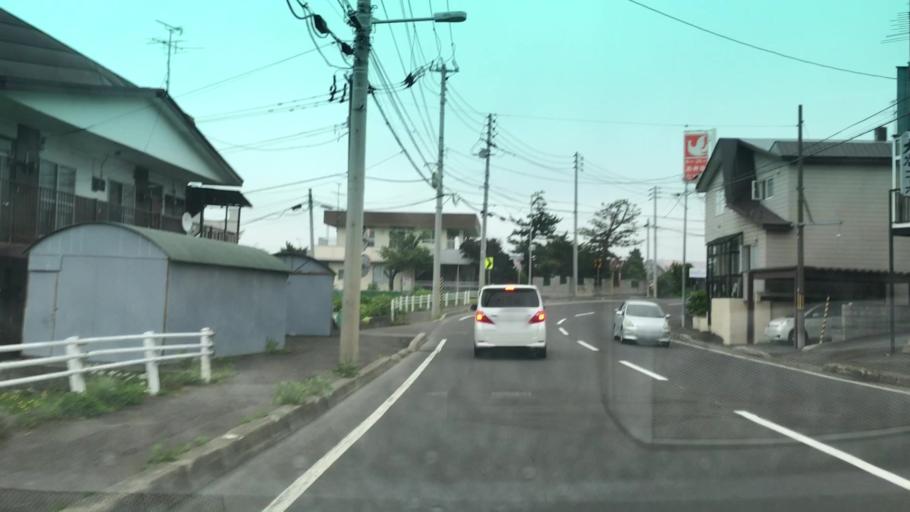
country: JP
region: Hokkaido
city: Sapporo
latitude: 43.0011
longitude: 141.3240
